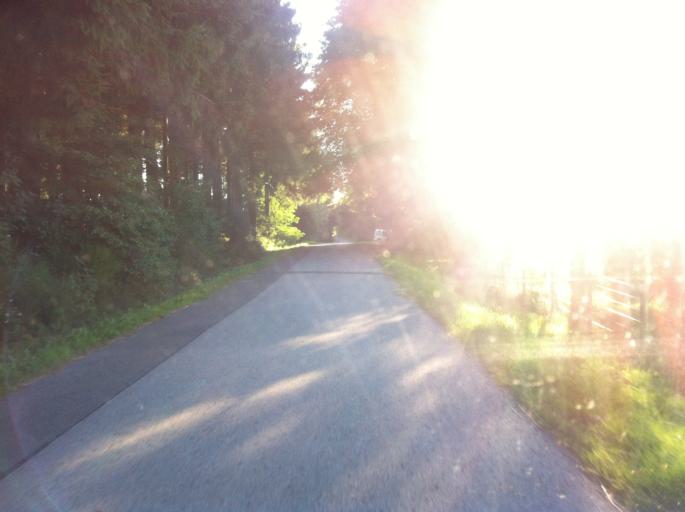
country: DE
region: Rheinland-Pfalz
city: Scheid
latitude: 50.4103
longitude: 6.3735
